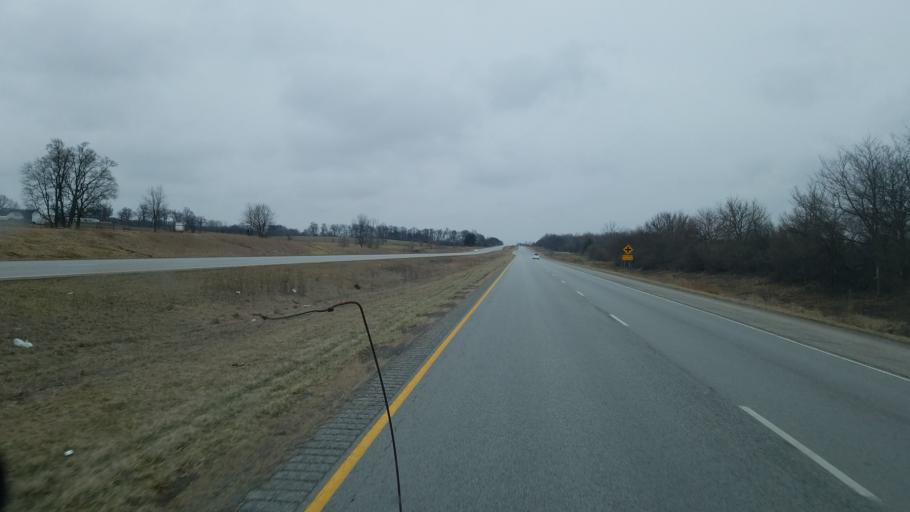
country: US
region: Indiana
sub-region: Fulton County
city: Rochester
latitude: 40.9508
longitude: -86.1686
